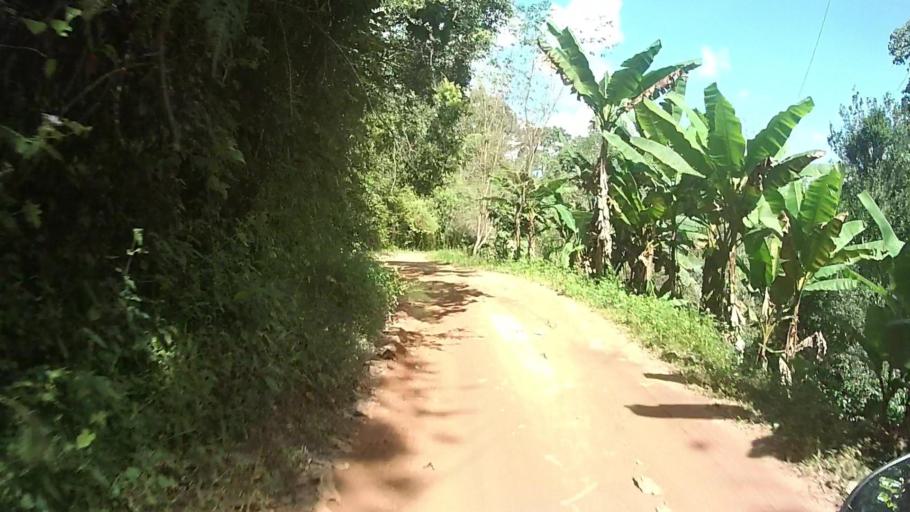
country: TH
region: Lampang
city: Mueang Pan
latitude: 18.9120
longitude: 99.4123
